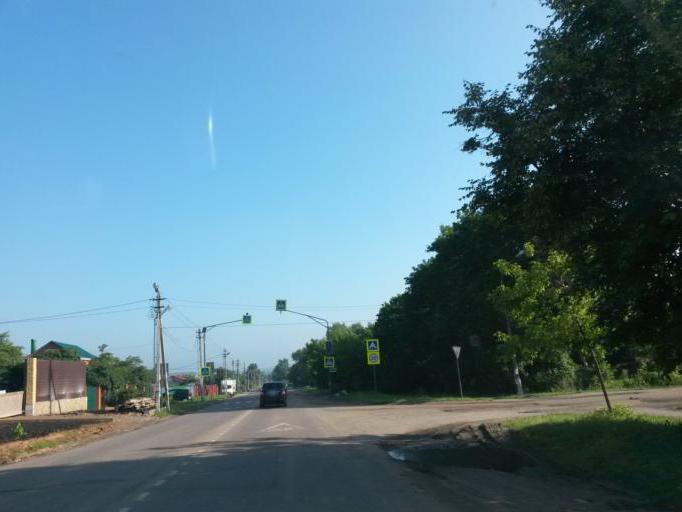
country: RU
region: Moskovskaya
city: Yam
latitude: 55.4761
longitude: 37.7530
